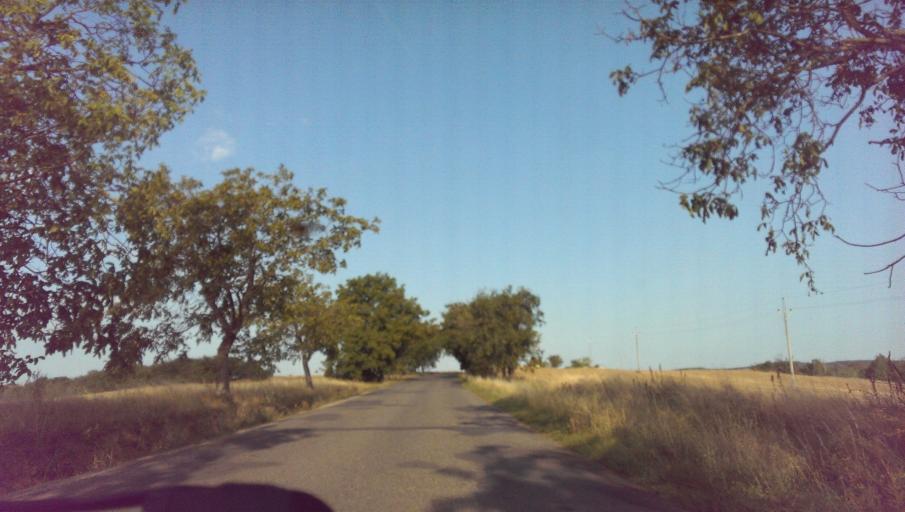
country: CZ
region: South Moravian
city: Zeravice
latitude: 49.0573
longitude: 17.2392
